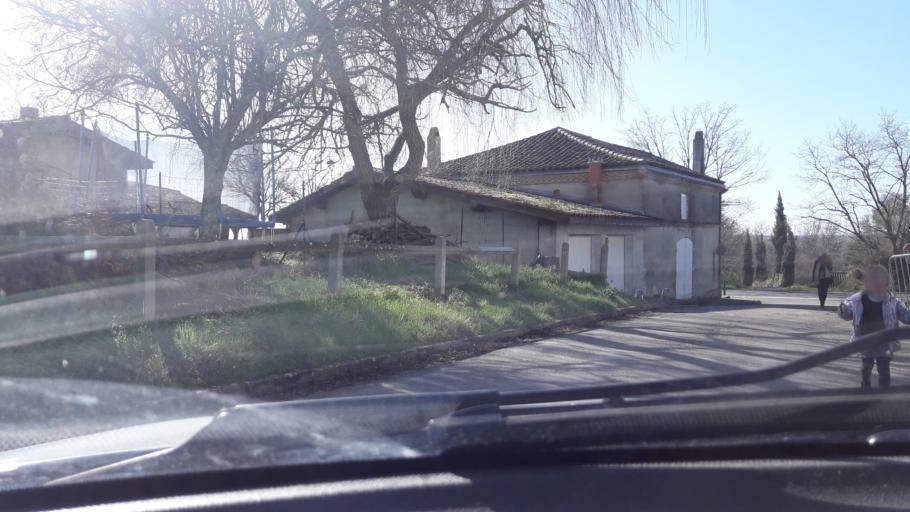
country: FR
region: Midi-Pyrenees
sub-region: Departement du Gers
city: Pujaudran
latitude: 43.6617
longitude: 1.0264
